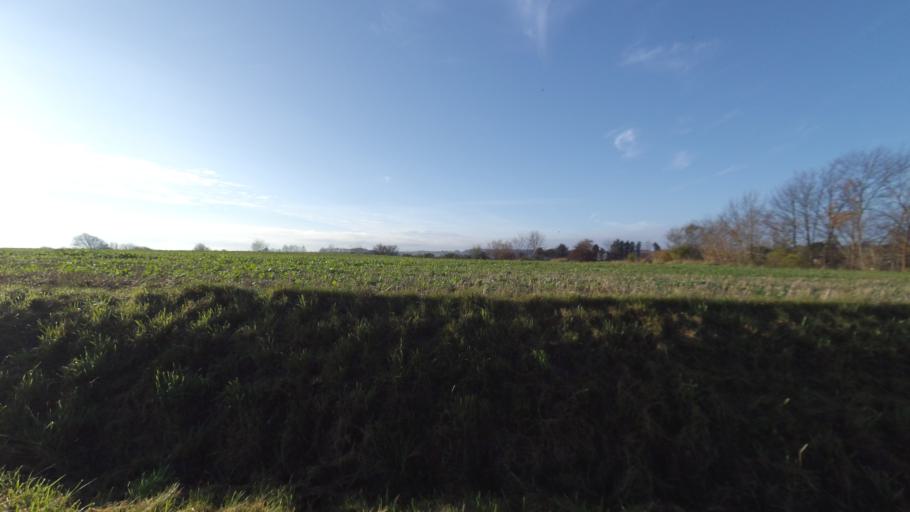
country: DK
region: Central Jutland
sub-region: Arhus Kommune
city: Beder
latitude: 56.0215
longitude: 10.2610
